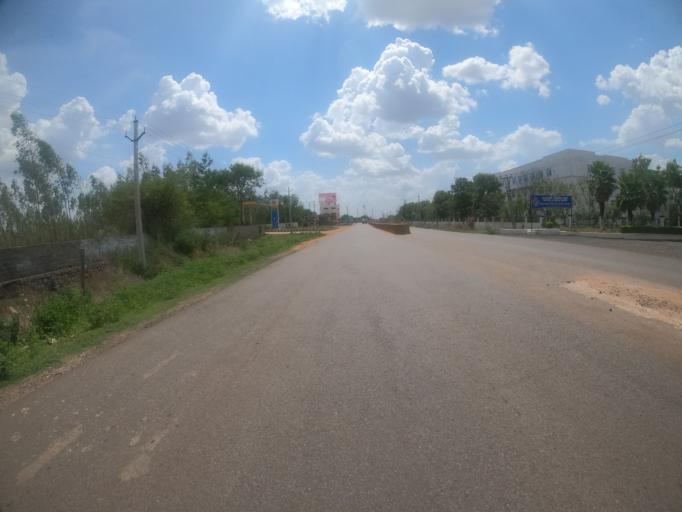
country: IN
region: Telangana
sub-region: Rangareddi
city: Sriramnagar
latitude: 17.3050
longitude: 78.1486
